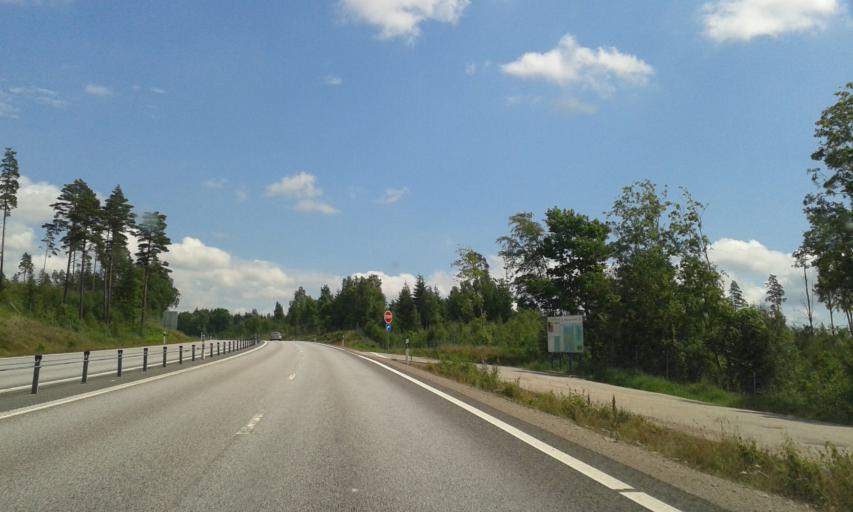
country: SE
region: Kronoberg
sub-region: Vaxjo Kommun
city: Gemla
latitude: 56.8965
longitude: 14.6884
